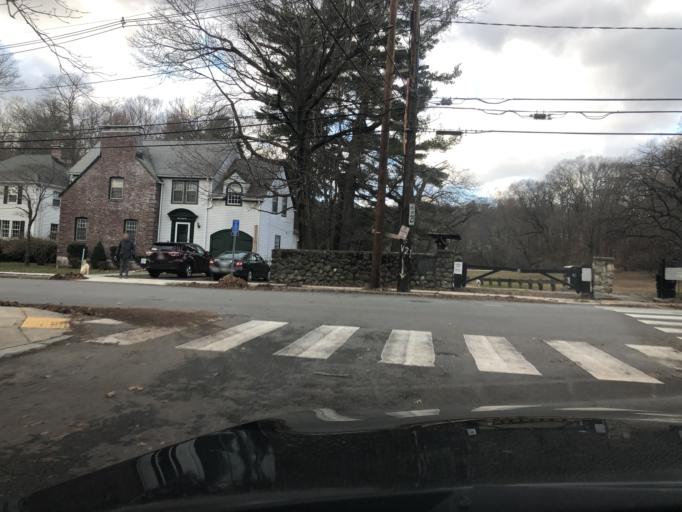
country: US
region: Massachusetts
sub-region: Middlesex County
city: Arlington
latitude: 42.4102
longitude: -71.1636
